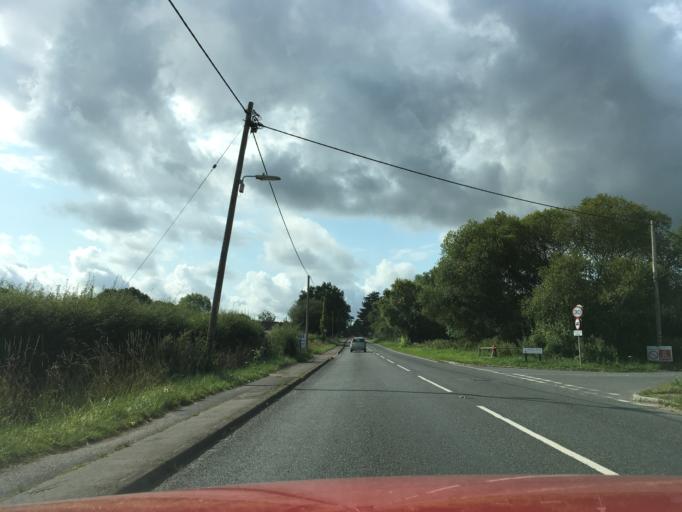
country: GB
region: England
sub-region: Hampshire
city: Bishops Waltham
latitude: 50.9413
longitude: -1.2025
